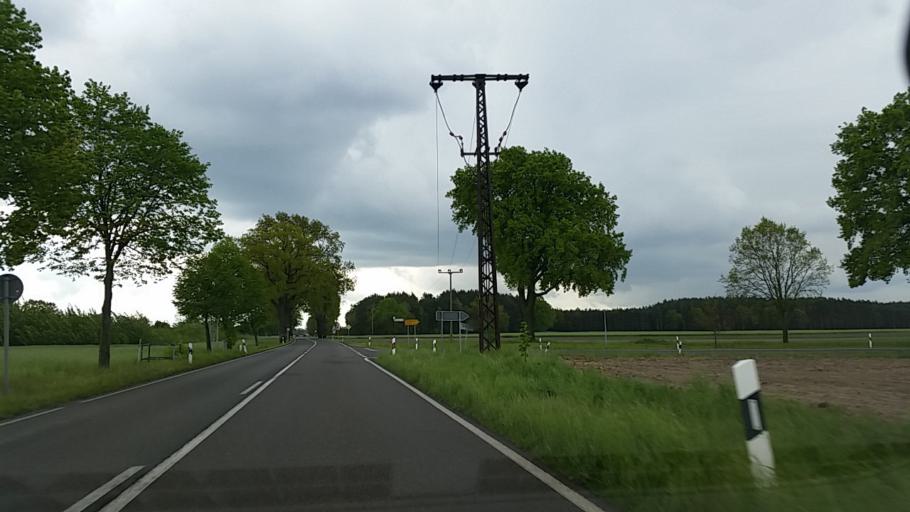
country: DE
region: Brandenburg
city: Storkow
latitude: 52.2738
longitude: 13.9149
